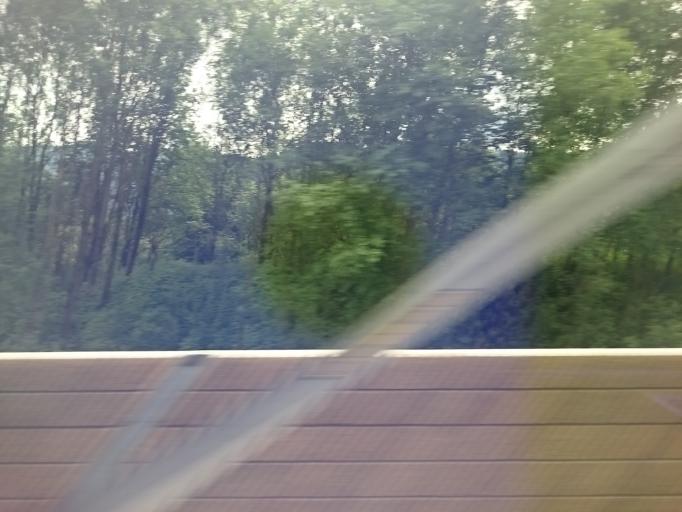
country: AT
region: Tyrol
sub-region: Politischer Bezirk Kufstein
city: Breitenbach am Inn
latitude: 47.4691
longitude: 11.9667
